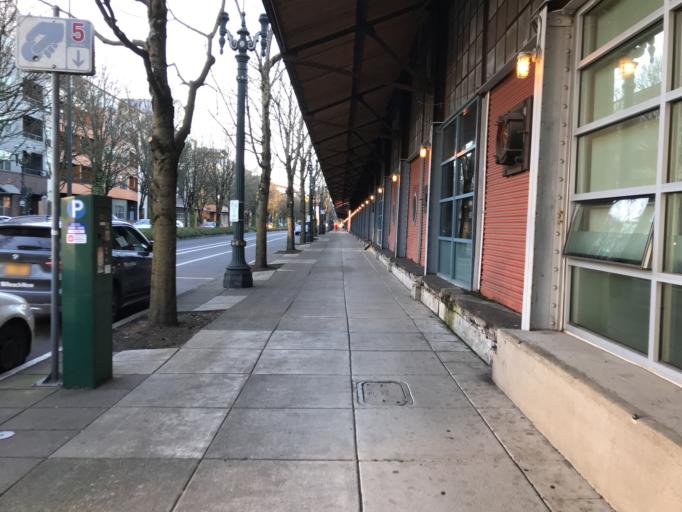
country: US
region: Oregon
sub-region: Multnomah County
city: Portland
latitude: 45.5283
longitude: -122.6732
